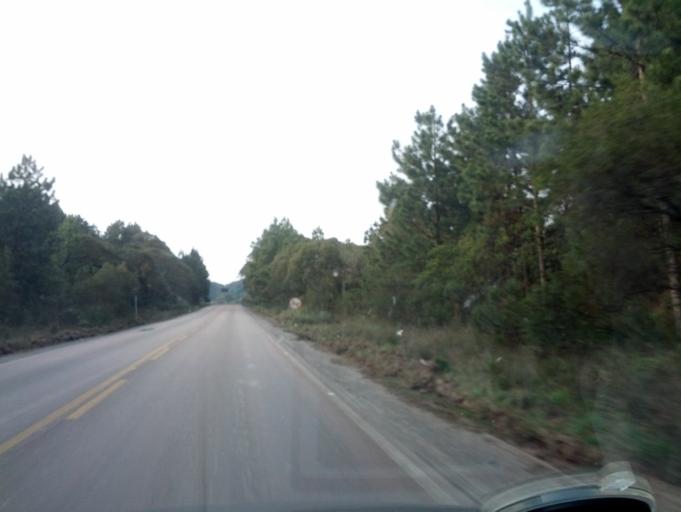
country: BR
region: Santa Catarina
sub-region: Otacilio Costa
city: Otacilio Costa
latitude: -27.3130
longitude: -50.1361
